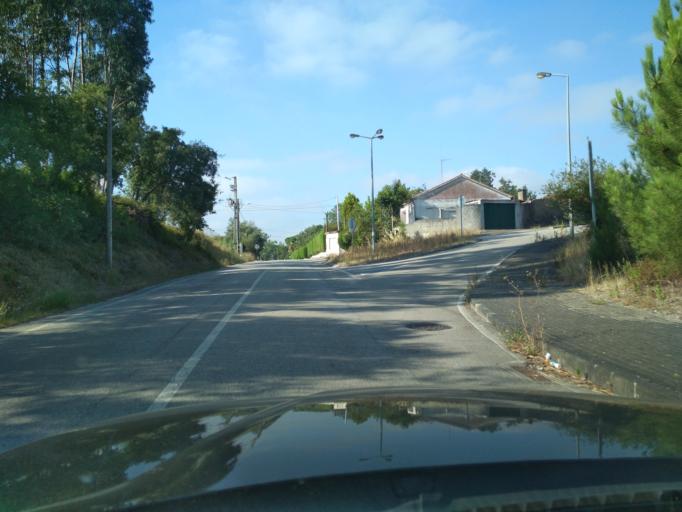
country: PT
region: Coimbra
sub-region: Condeixa-A-Nova
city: Condeixa-a-Nova
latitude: 40.1444
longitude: -8.4676
